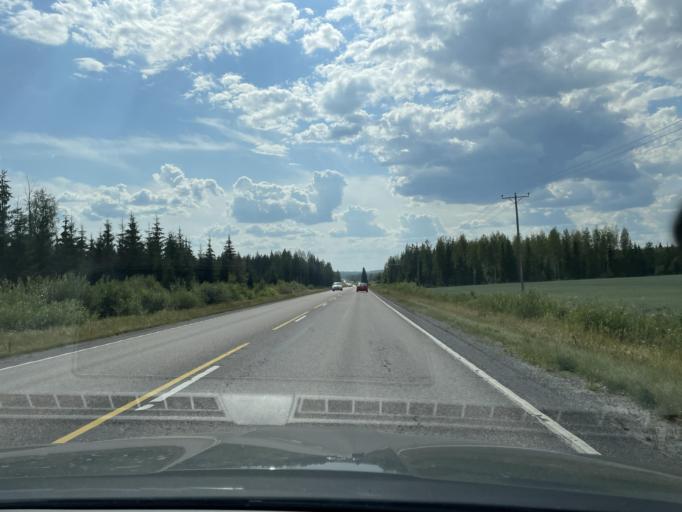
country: FI
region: Central Finland
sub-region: Jyvaeskylae
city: Korpilahti
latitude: 61.9839
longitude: 25.4135
